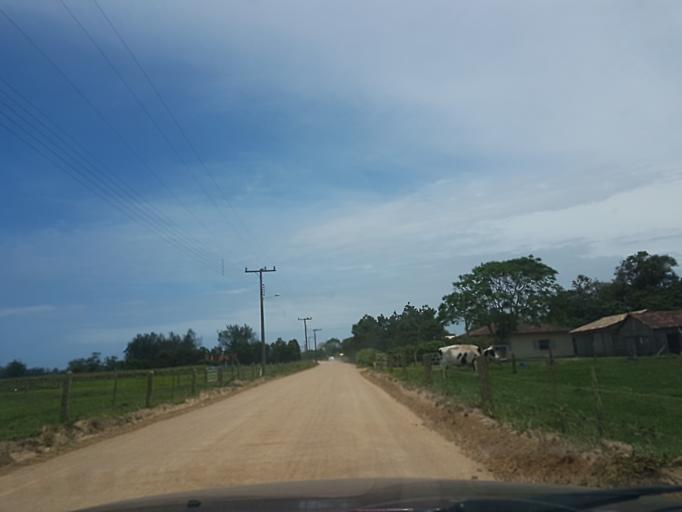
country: BR
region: Santa Catarina
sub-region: Jaguaruna
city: Jaguaruna
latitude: -28.6386
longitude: -48.9610
